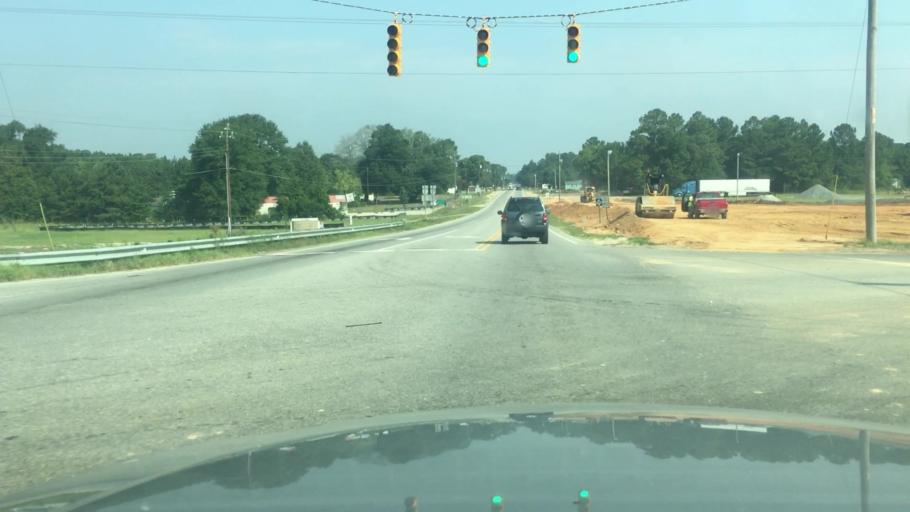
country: US
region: North Carolina
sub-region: Cumberland County
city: Hope Mills
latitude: 34.9457
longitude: -78.9317
